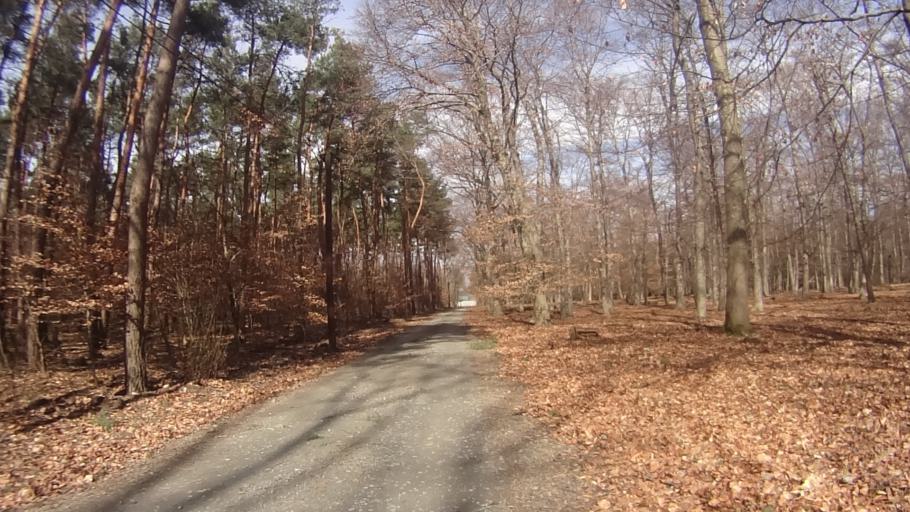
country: DE
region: Hesse
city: Kelsterbach
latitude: 50.0328
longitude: 8.5018
